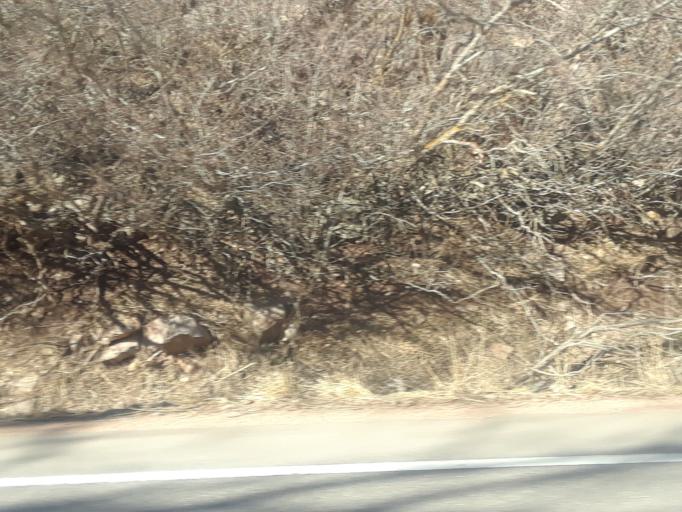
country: US
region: Colorado
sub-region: Boulder County
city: Lyons
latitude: 40.1322
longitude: -105.2924
